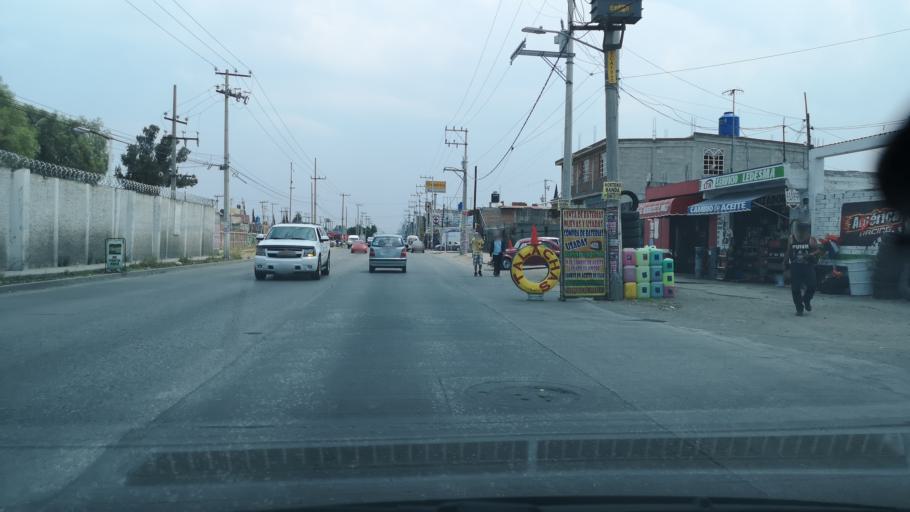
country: MX
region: Mexico
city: Ecatepec
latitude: 19.6326
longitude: -99.0535
